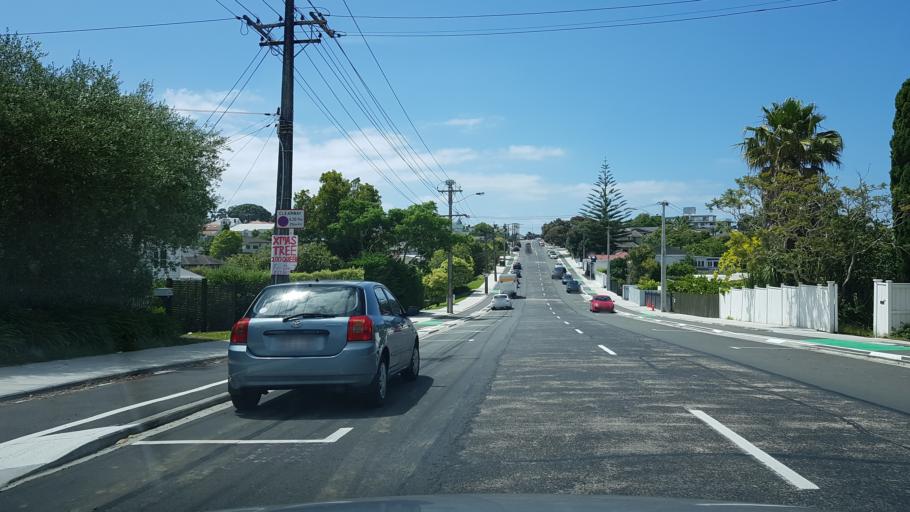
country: NZ
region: Auckland
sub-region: Auckland
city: North Shore
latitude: -36.8151
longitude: 174.7454
